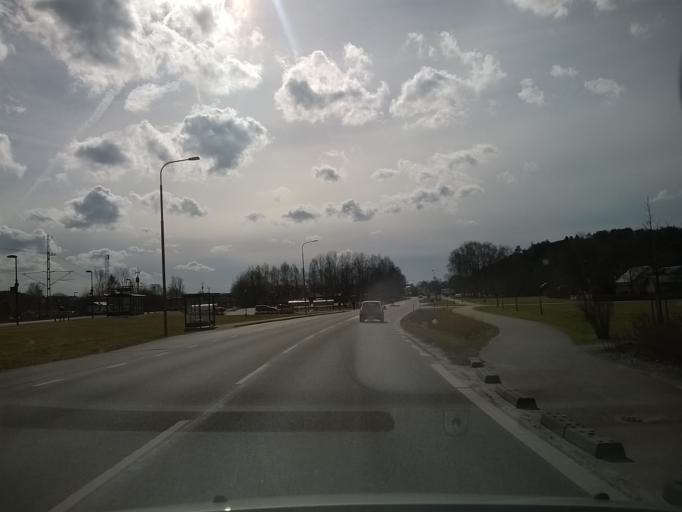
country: SE
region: Vaestra Goetaland
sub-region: Stenungsunds Kommun
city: Stora Hoga
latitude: 58.0202
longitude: 11.8361
